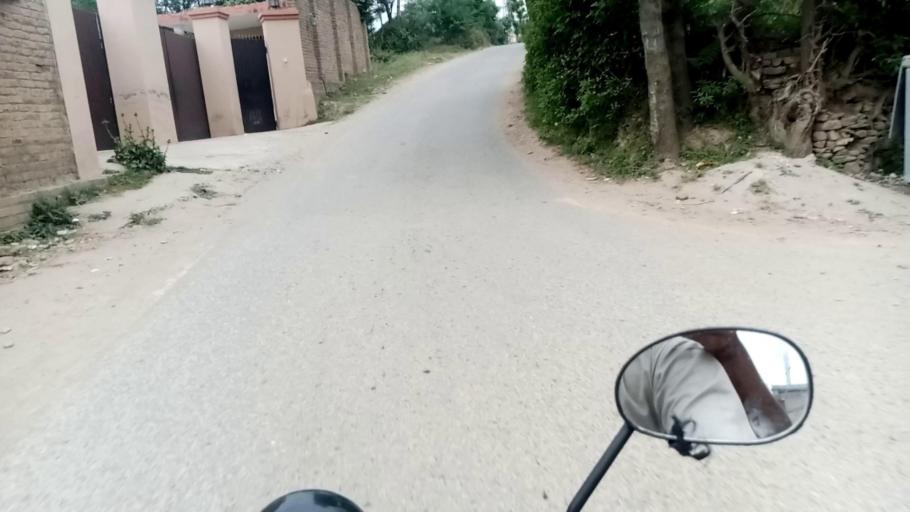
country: PK
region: Khyber Pakhtunkhwa
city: Mingora
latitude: 34.7580
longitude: 72.3787
